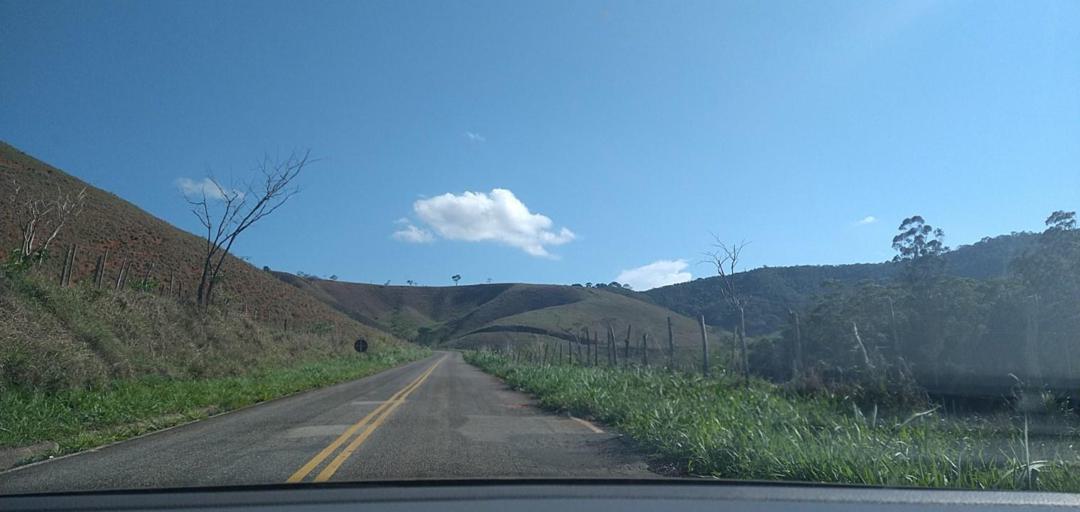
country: BR
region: Minas Gerais
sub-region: Alvinopolis
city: Alvinopolis
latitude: -20.1884
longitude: -42.9380
